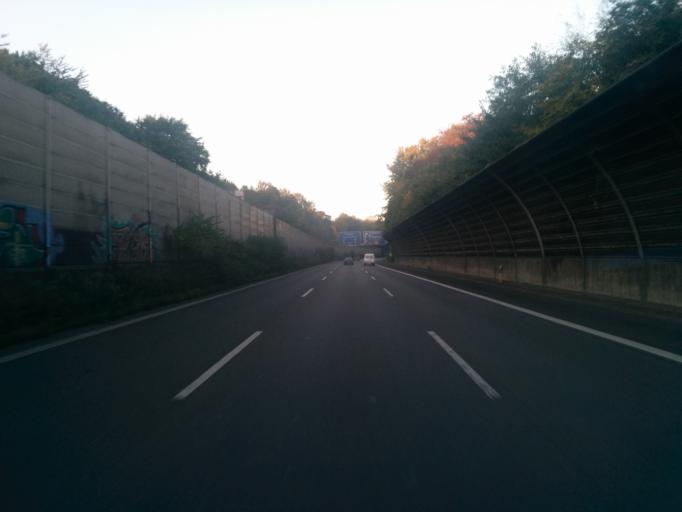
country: DE
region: North Rhine-Westphalia
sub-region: Regierungsbezirk Dusseldorf
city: Essen
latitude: 51.4263
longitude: 7.0121
